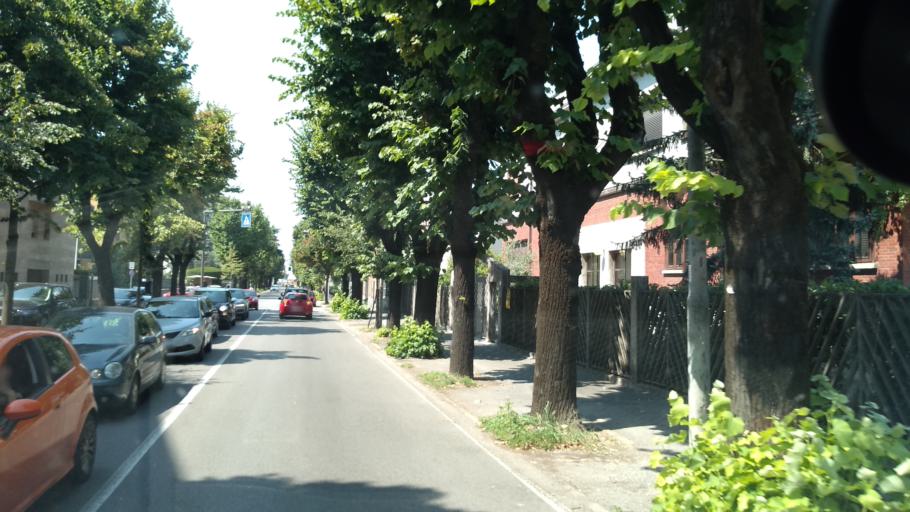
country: IT
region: Lombardy
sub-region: Provincia di Bergamo
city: Treviglio
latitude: 45.5172
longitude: 9.5929
